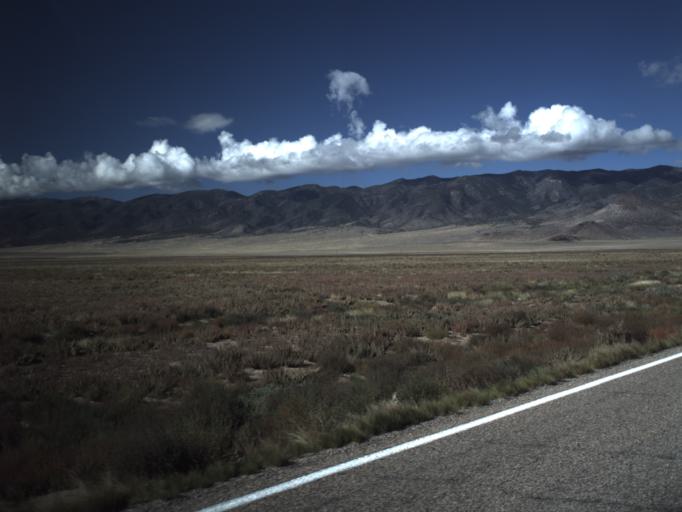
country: US
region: Utah
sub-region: Beaver County
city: Milford
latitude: 38.4700
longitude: -113.4053
